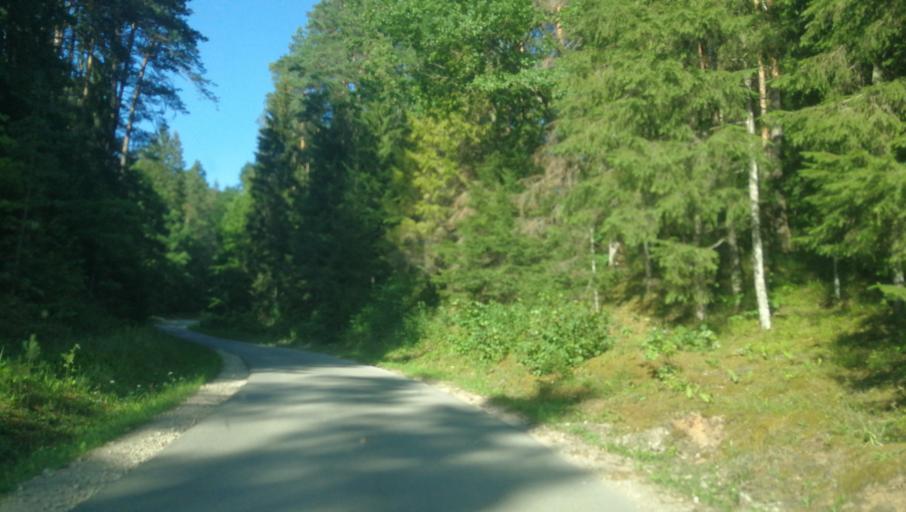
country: LV
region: Cesu Rajons
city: Cesis
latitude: 57.2848
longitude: 25.2137
